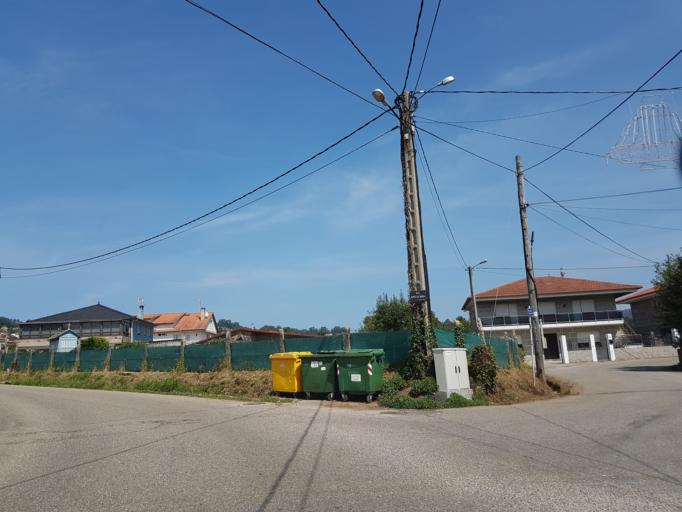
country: ES
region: Galicia
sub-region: Provincia de Pontevedra
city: Porrino
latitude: 42.2105
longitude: -8.6192
